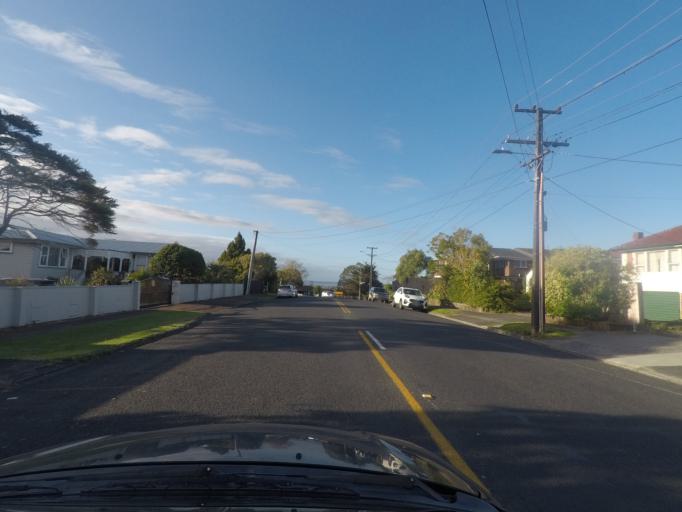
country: NZ
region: Auckland
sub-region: Auckland
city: Waitakere
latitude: -36.9138
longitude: 174.6583
